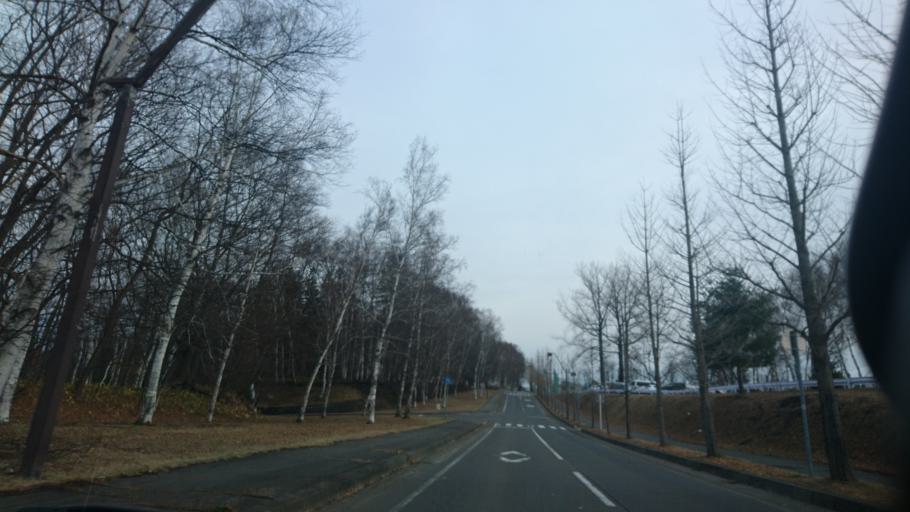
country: JP
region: Hokkaido
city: Otofuke
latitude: 42.9951
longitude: 143.1954
